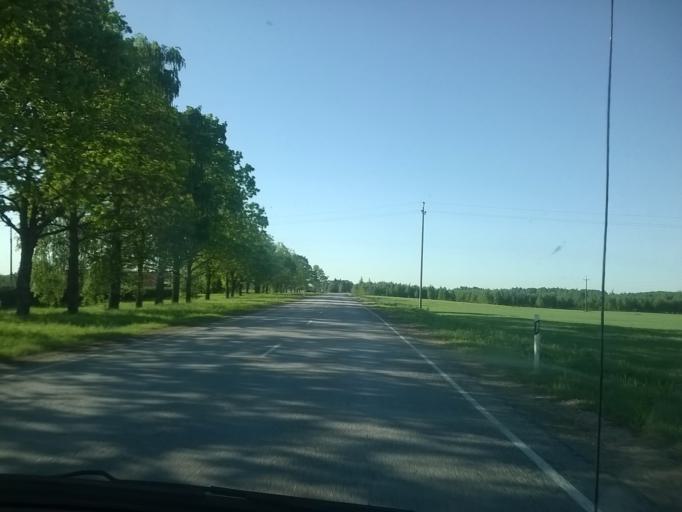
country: EE
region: Valgamaa
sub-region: Valga linn
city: Valga
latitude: 57.9338
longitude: 26.1713
